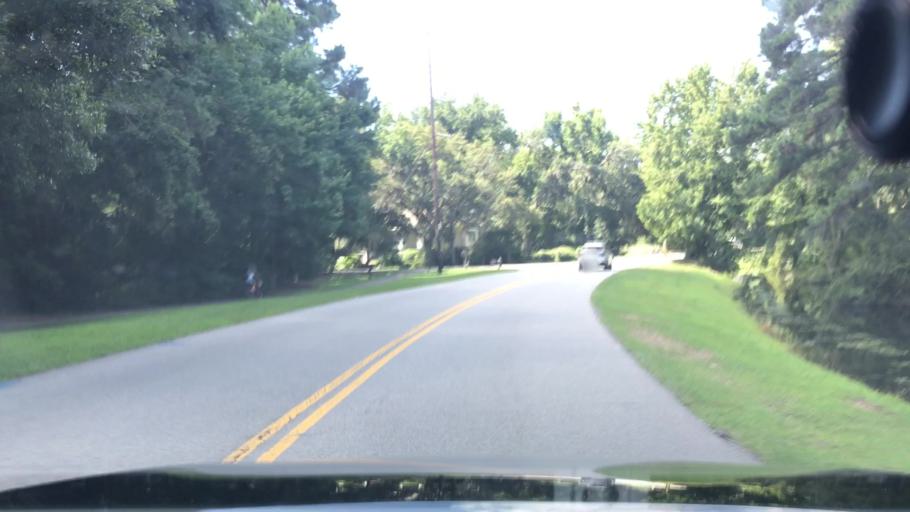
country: US
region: South Carolina
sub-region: Beaufort County
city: Hilton Head Island
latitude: 32.1383
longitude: -80.7877
